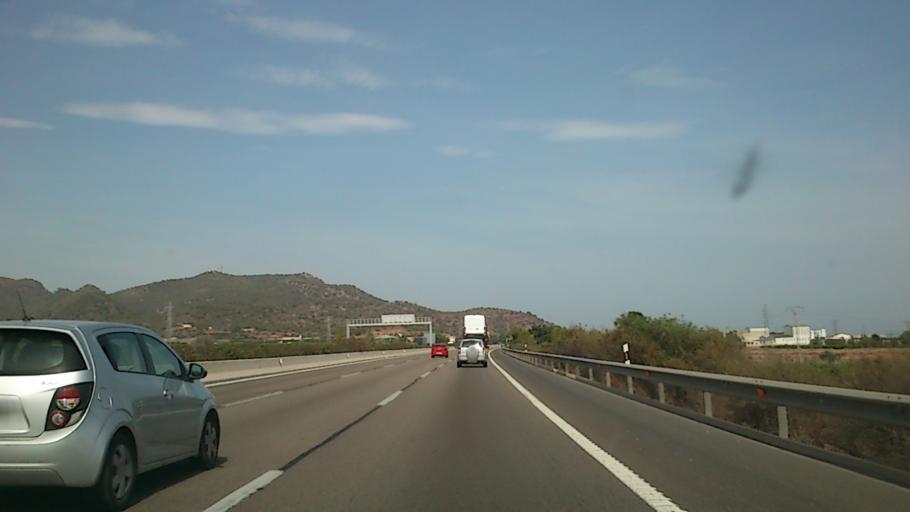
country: ES
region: Valencia
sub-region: Provincia de Valencia
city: Pucol
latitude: 39.6146
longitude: -0.3398
